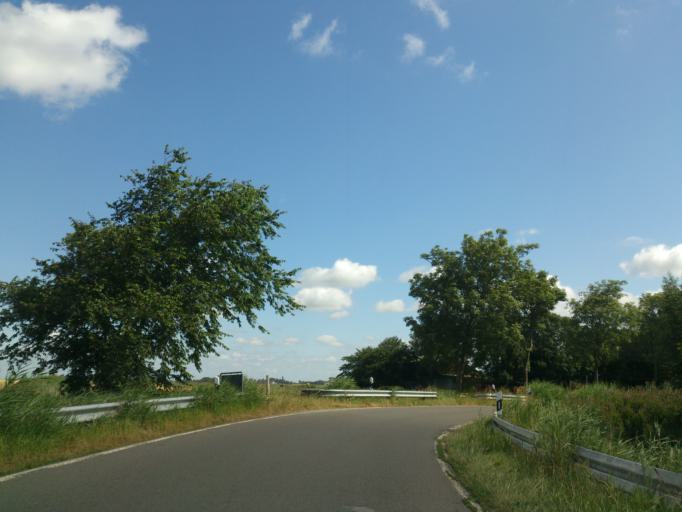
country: DE
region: Schleswig-Holstein
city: Katharinenheerd
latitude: 54.3151
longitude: 8.8543
